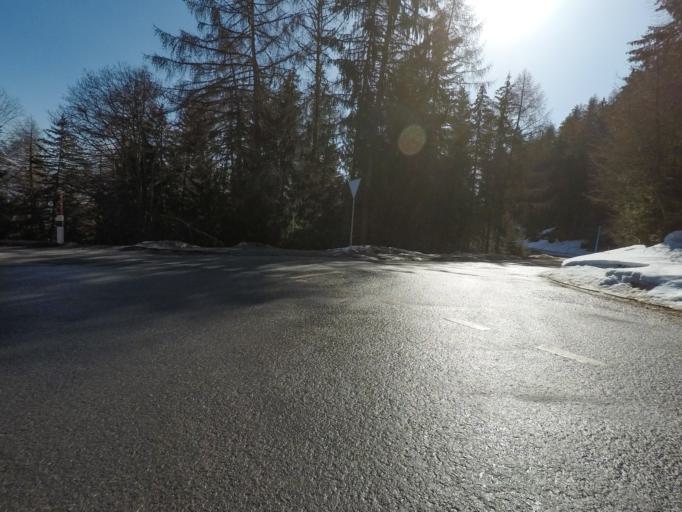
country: CH
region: Valais
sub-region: Herens District
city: Vex
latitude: 46.1962
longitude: 7.3862
